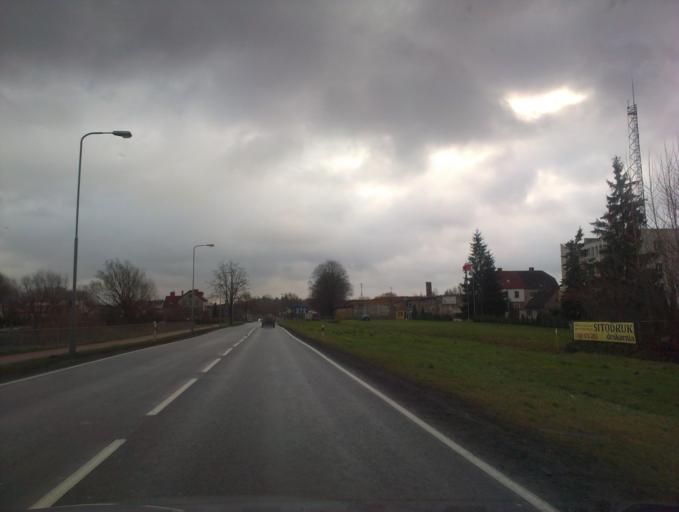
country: PL
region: West Pomeranian Voivodeship
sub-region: Powiat szczecinecki
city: Szczecinek
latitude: 53.7168
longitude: 16.6936
